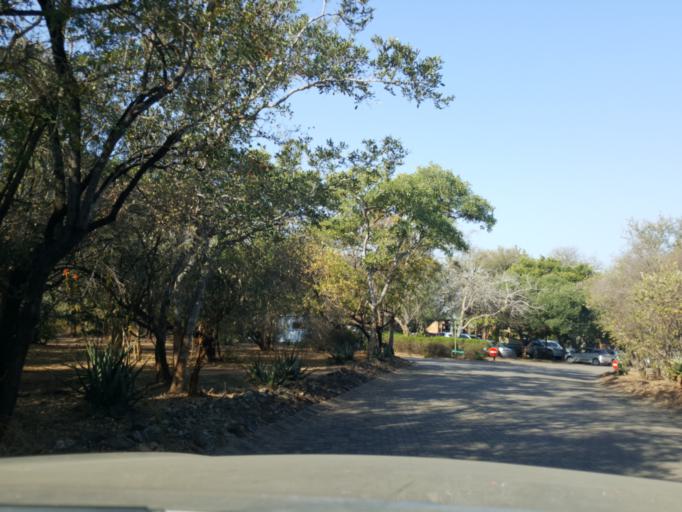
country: SZ
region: Hhohho
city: Ntfonjeni
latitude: -25.4266
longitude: 31.4488
